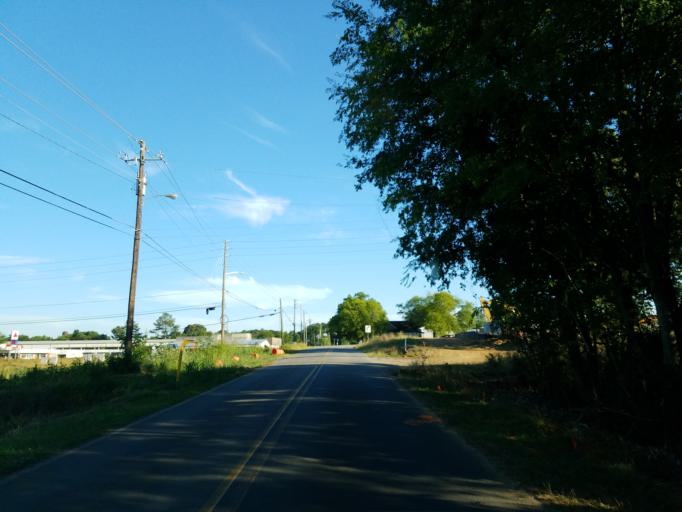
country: US
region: Georgia
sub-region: Bartow County
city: Adairsville
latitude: 34.3781
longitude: -84.9353
